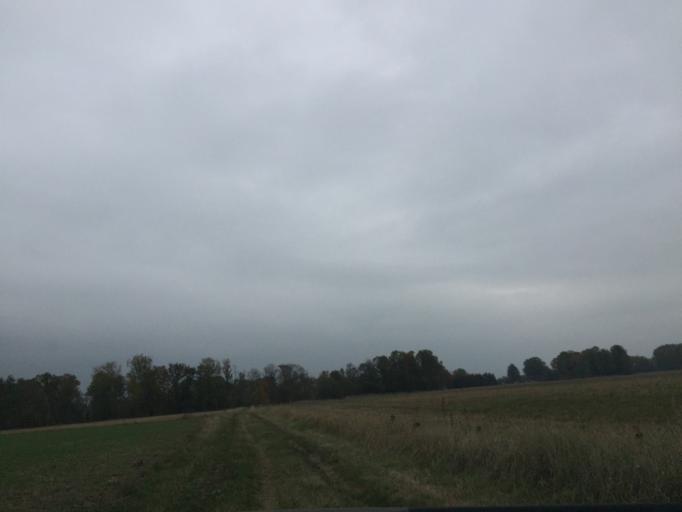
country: LV
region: Dobeles Rajons
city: Dobele
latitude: 56.6755
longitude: 23.4374
